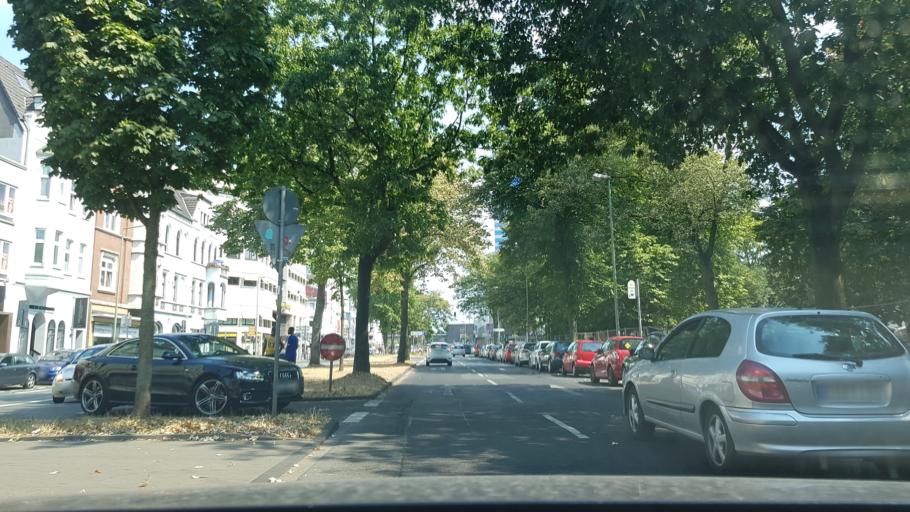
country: DE
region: North Rhine-Westphalia
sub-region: Regierungsbezirk Dusseldorf
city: Duisburg
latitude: 51.4309
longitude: 6.7671
